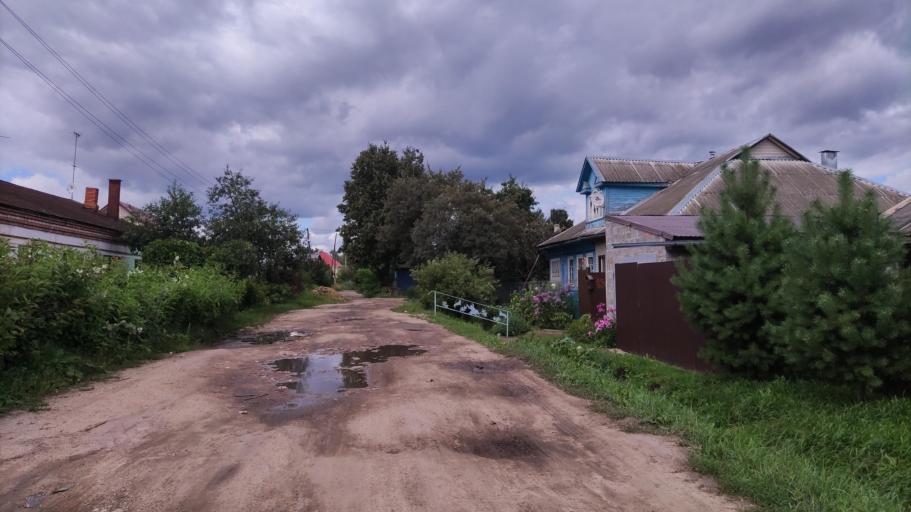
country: RU
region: Tverskaya
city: Rzhev
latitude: 56.2442
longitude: 34.2941
